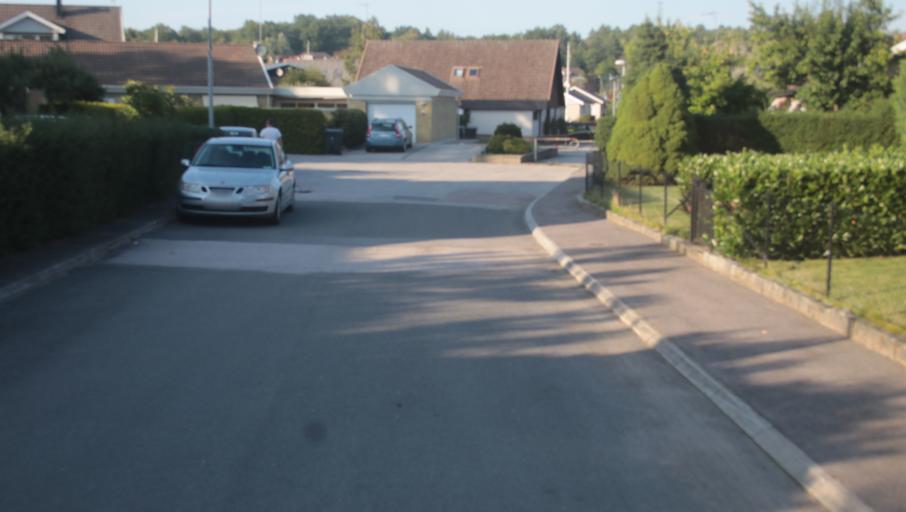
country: SE
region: Blekinge
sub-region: Karlshamns Kommun
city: Karlshamn
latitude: 56.1839
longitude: 14.8594
